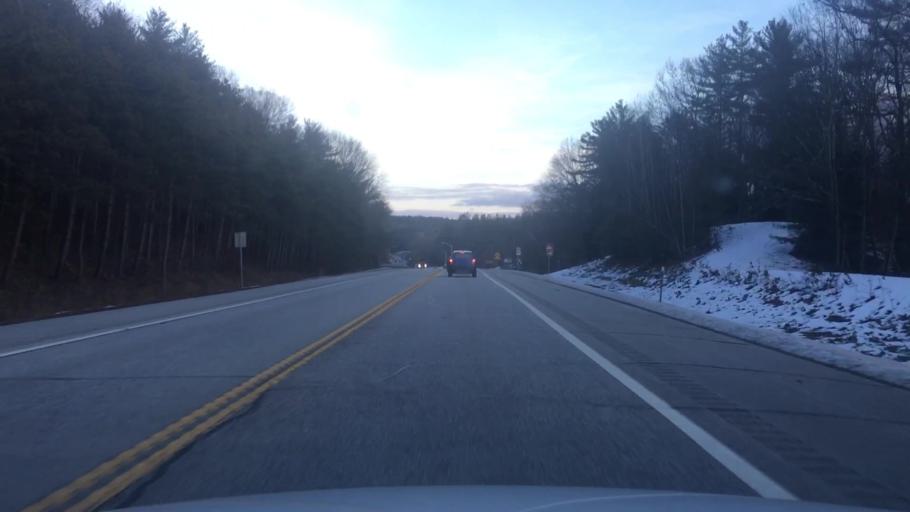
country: US
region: New Hampshire
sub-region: Merrimack County
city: Contoocook
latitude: 43.1799
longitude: -71.7598
